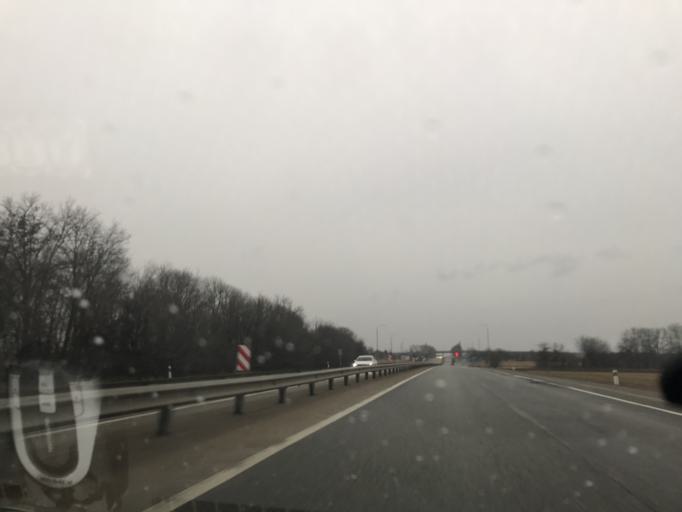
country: RU
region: Krasnodarskiy
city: Pavlovskaya
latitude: 46.2191
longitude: 39.8315
